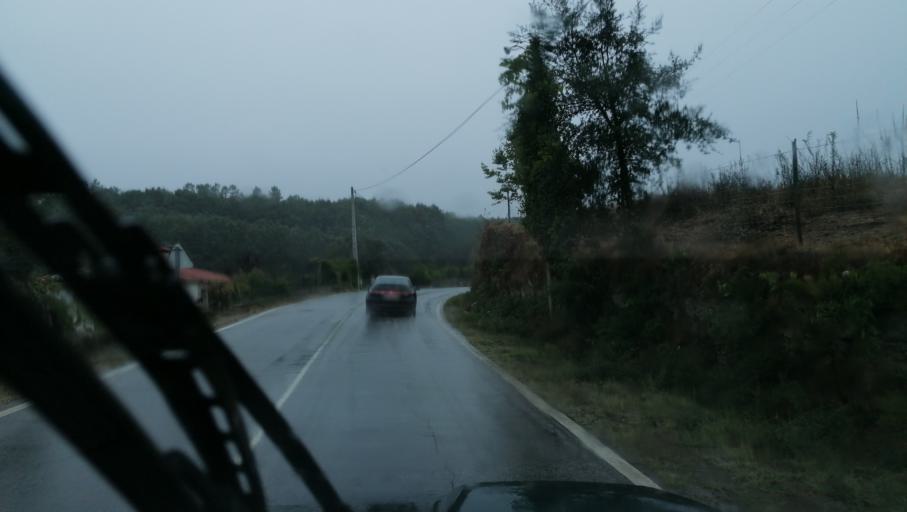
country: PT
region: Braga
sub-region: Cabeceiras de Basto
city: Cabeceiras de Basto
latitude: 41.4992
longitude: -7.9067
